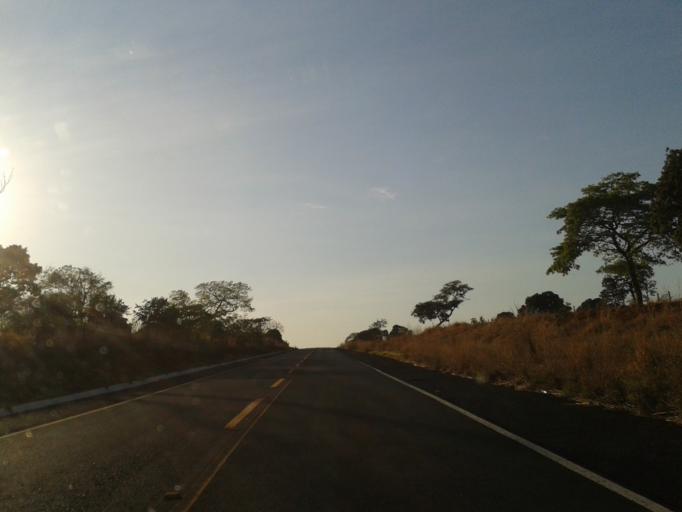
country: BR
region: Minas Gerais
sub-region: Santa Vitoria
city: Santa Vitoria
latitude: -19.1310
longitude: -50.2486
